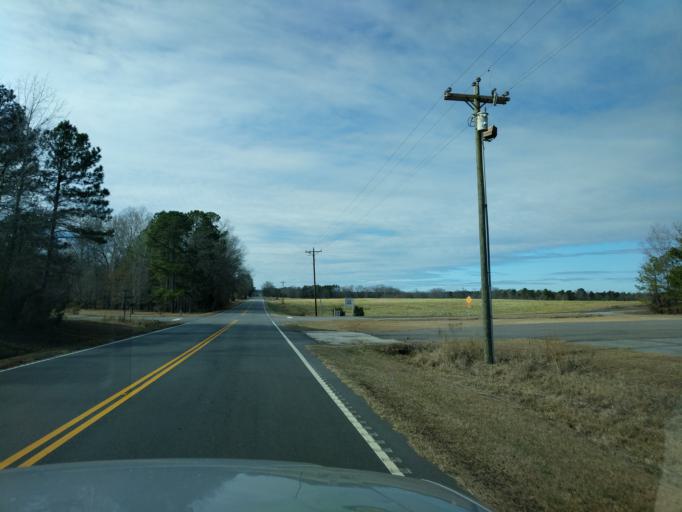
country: US
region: South Carolina
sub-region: Edgefield County
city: Edgefield
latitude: 33.9368
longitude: -81.9512
